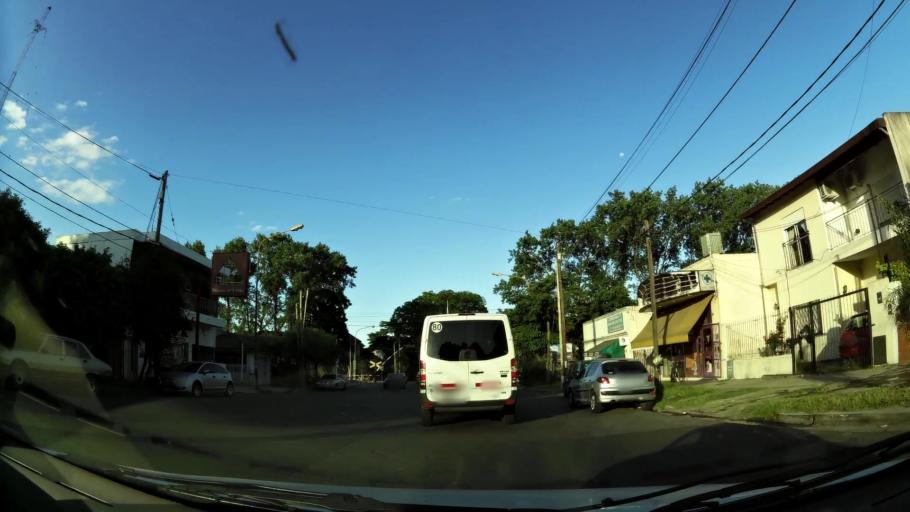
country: AR
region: Buenos Aires
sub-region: Partido de General San Martin
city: General San Martin
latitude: -34.5677
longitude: -58.5380
